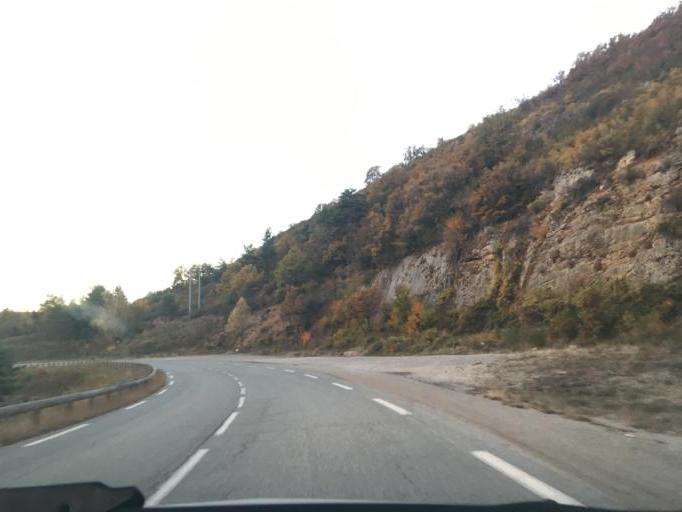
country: FR
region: Provence-Alpes-Cote d'Azur
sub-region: Departement du Var
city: Bargemon
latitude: 43.6889
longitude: 6.5073
